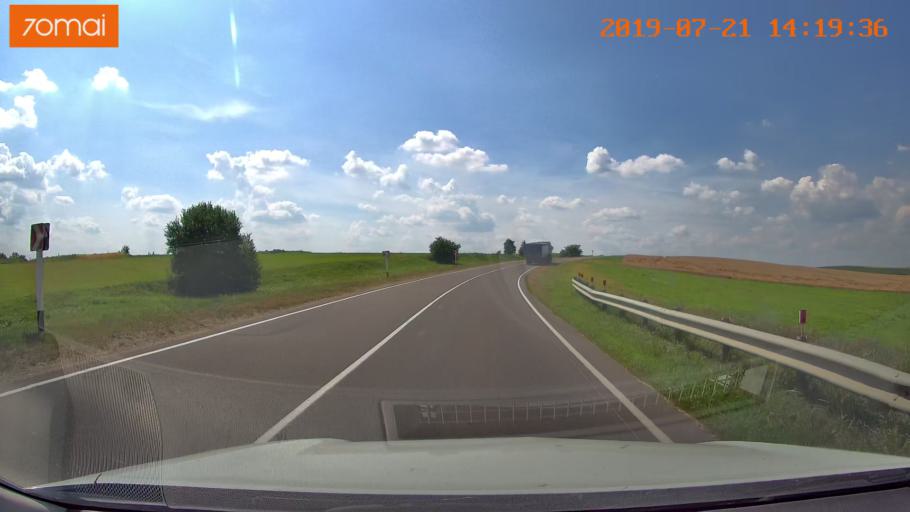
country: BY
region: Grodnenskaya
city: Karelichy
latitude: 53.5867
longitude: 26.1691
